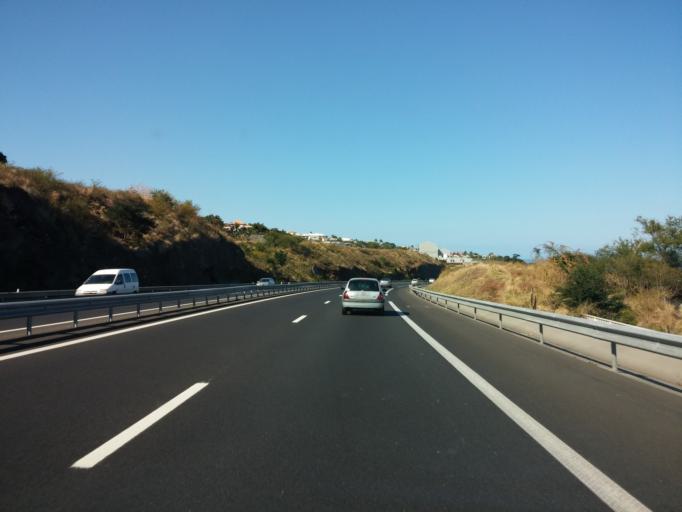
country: RE
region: Reunion
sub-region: Reunion
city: Saint-Leu
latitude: -21.1941
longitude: 55.2962
